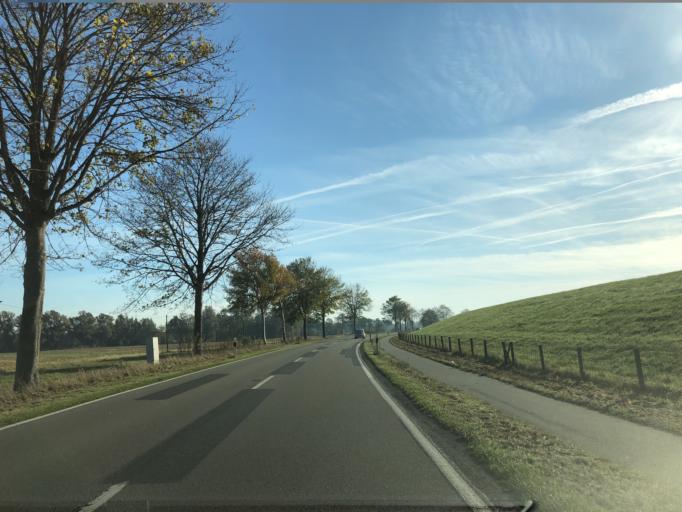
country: DE
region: Lower Saxony
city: Rhede
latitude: 53.0558
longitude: 7.3132
